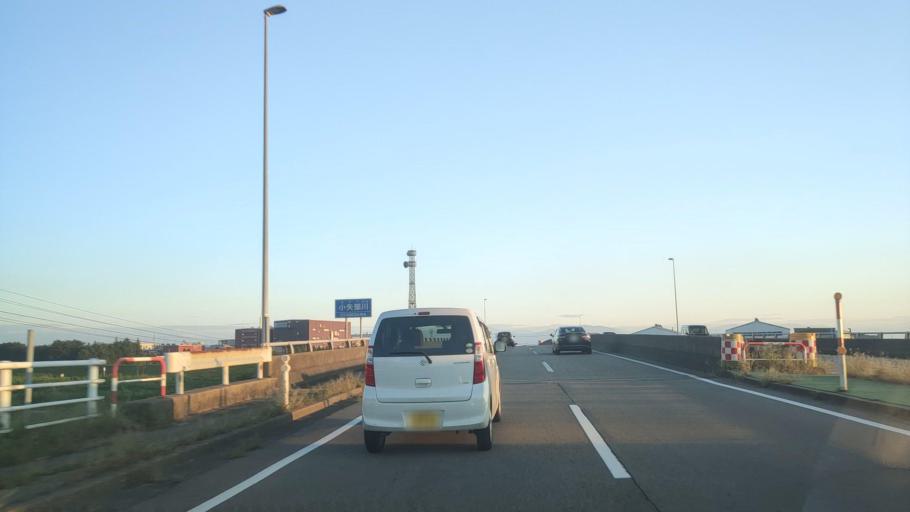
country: JP
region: Toyama
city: Takaoka
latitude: 36.7758
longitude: 137.0000
